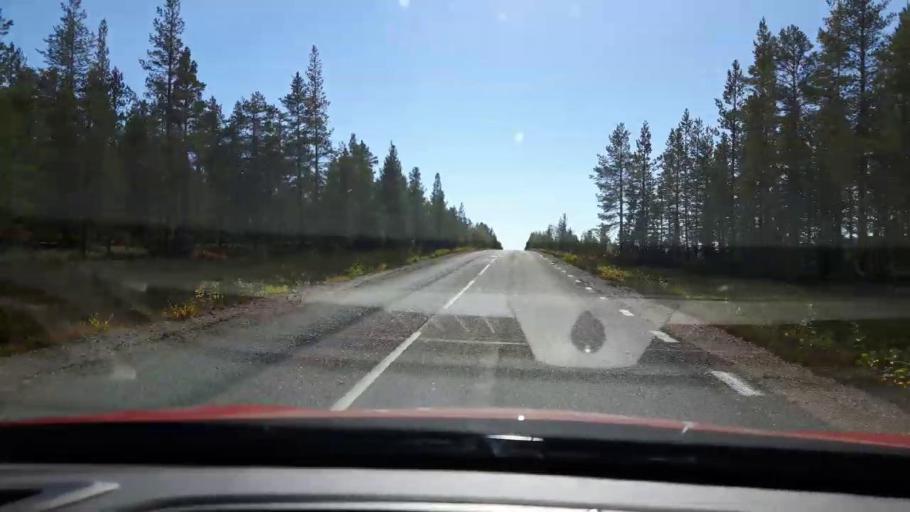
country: SE
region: Jaemtland
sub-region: Harjedalens Kommun
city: Sveg
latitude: 61.7327
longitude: 14.1643
